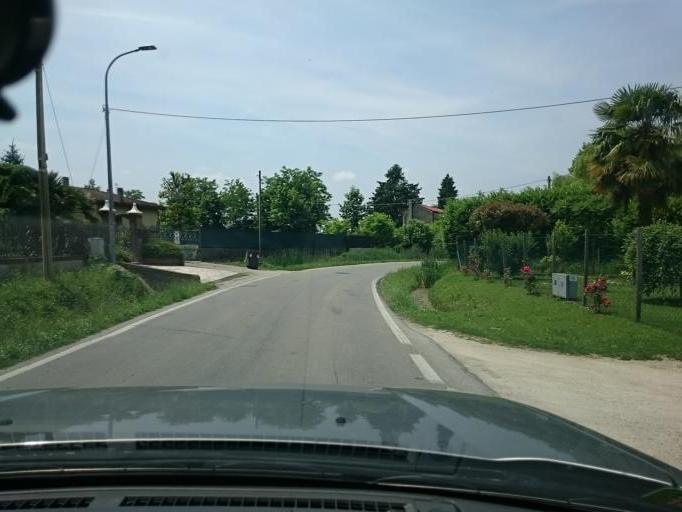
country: IT
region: Veneto
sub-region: Provincia di Padova
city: Legnaro
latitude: 45.3272
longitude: 11.9723
